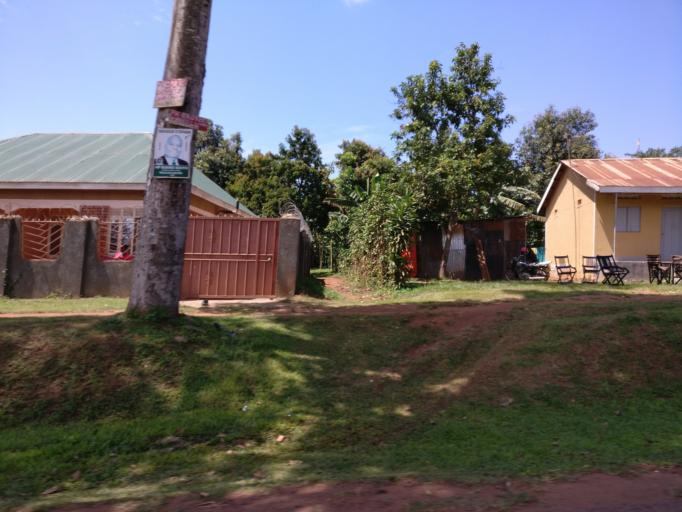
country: UG
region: Central Region
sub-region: Wakiso District
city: Kajansi
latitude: 0.1304
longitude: 32.5331
